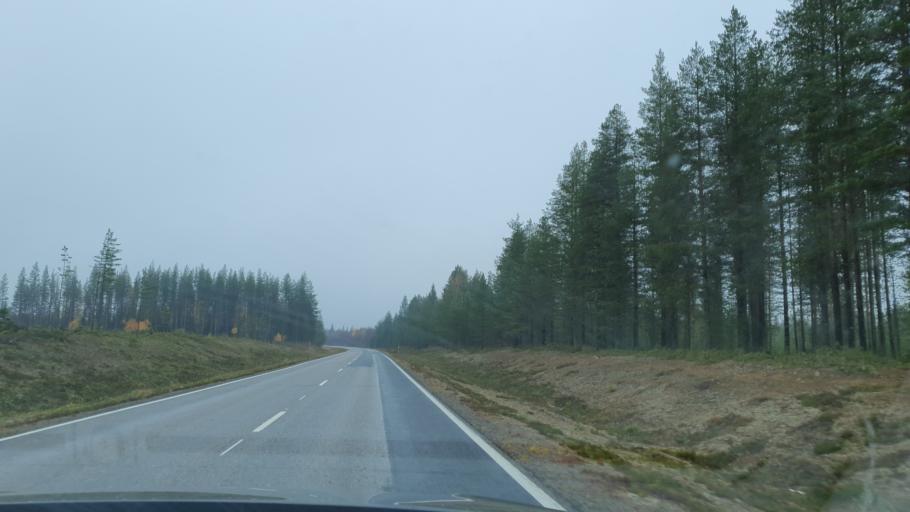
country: FI
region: Lapland
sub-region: Tunturi-Lappi
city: Kittilae
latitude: 67.4027
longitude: 24.9177
